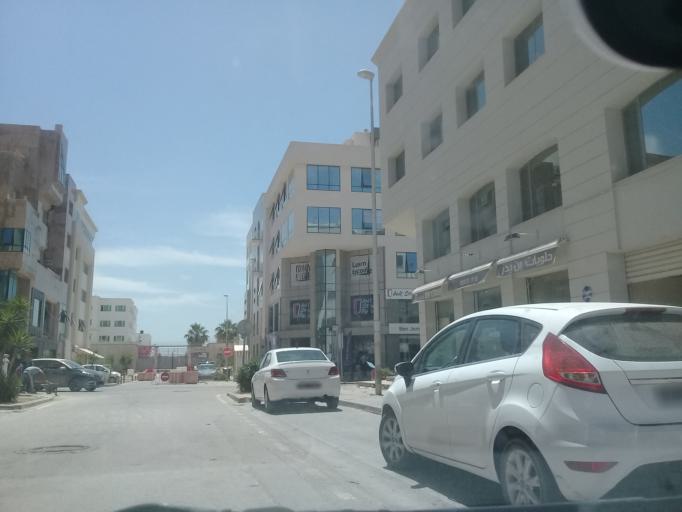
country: TN
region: Ariana
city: Ariana
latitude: 36.8345
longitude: 10.2411
